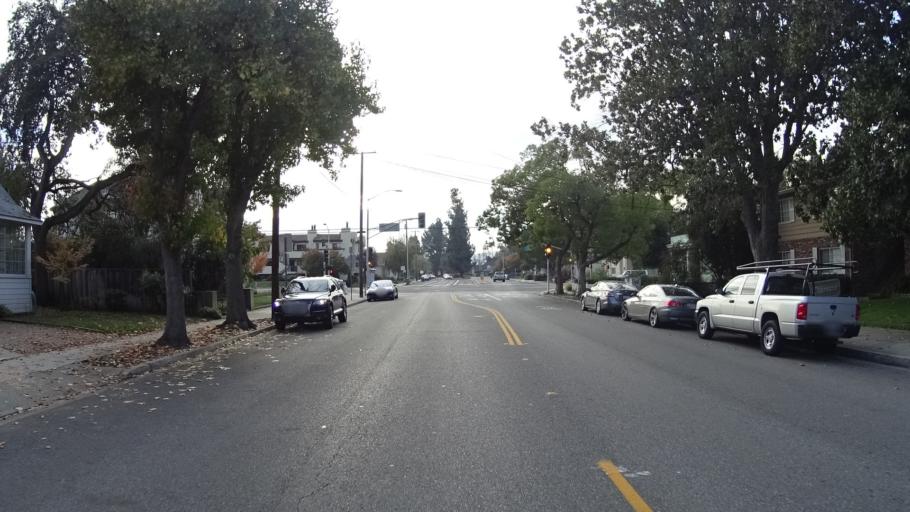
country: US
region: California
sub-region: Santa Clara County
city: Santa Clara
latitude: 37.3465
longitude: -121.9505
